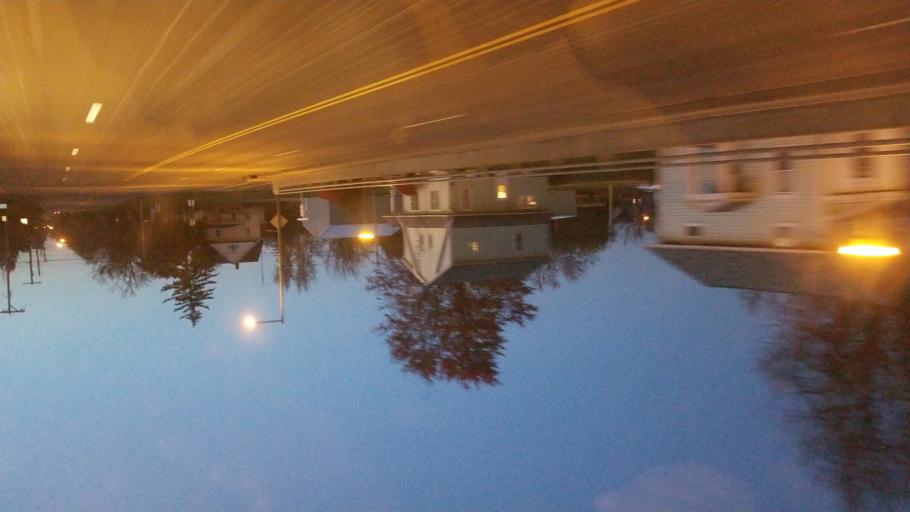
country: US
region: Ohio
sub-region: Crawford County
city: Crestline
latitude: 40.7804
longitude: -82.7382
